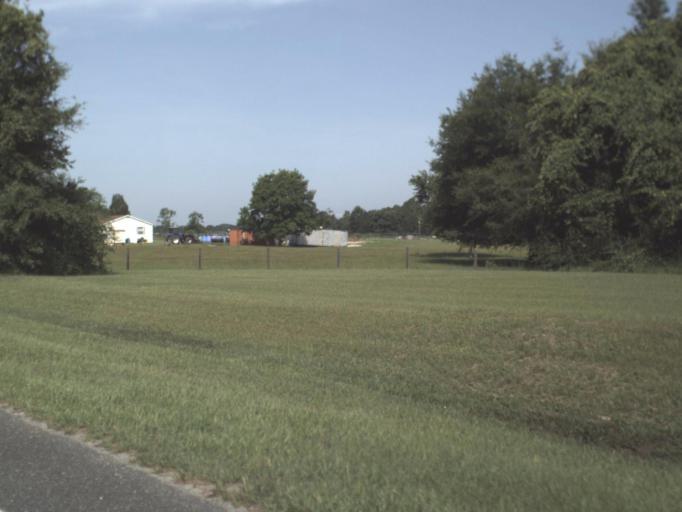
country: US
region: Florida
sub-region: Lafayette County
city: Mayo
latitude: 30.1876
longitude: -83.1262
